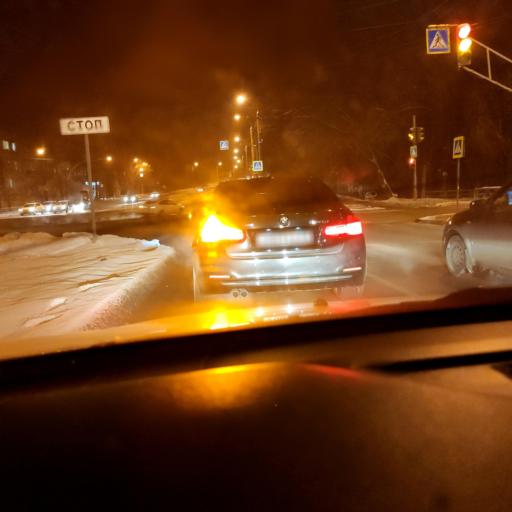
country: RU
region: Samara
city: Samara
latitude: 53.2234
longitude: 50.2371
